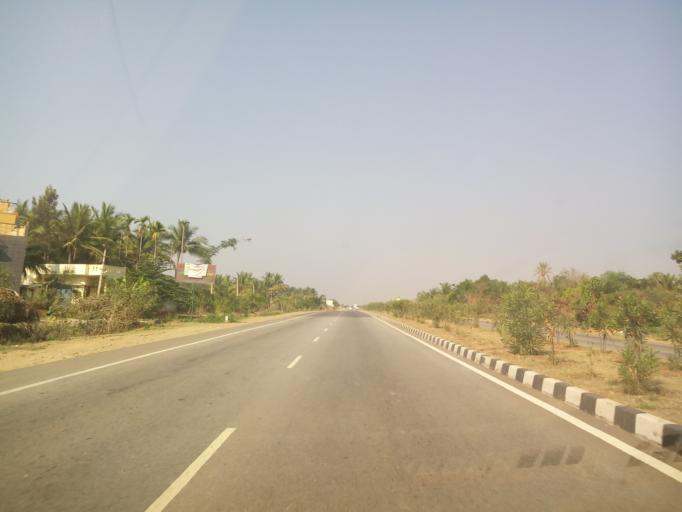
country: IN
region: Karnataka
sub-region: Tumkur
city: Kunigal
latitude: 13.0381
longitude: 77.1017
